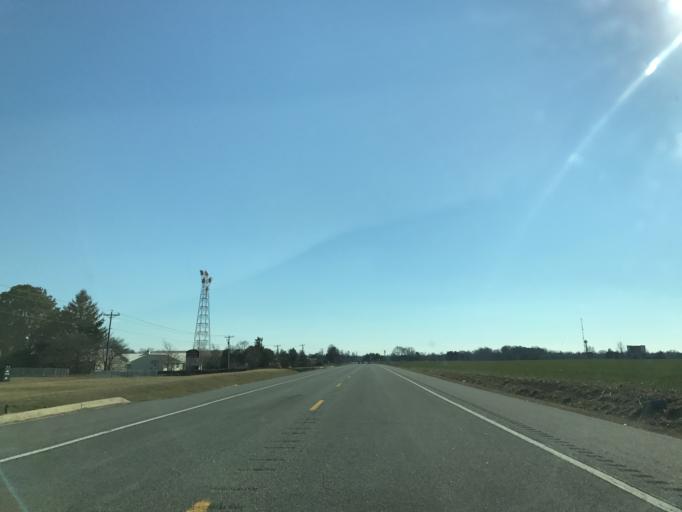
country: US
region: Maryland
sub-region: Queen Anne's County
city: Centreville
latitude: 38.9610
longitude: -76.0781
